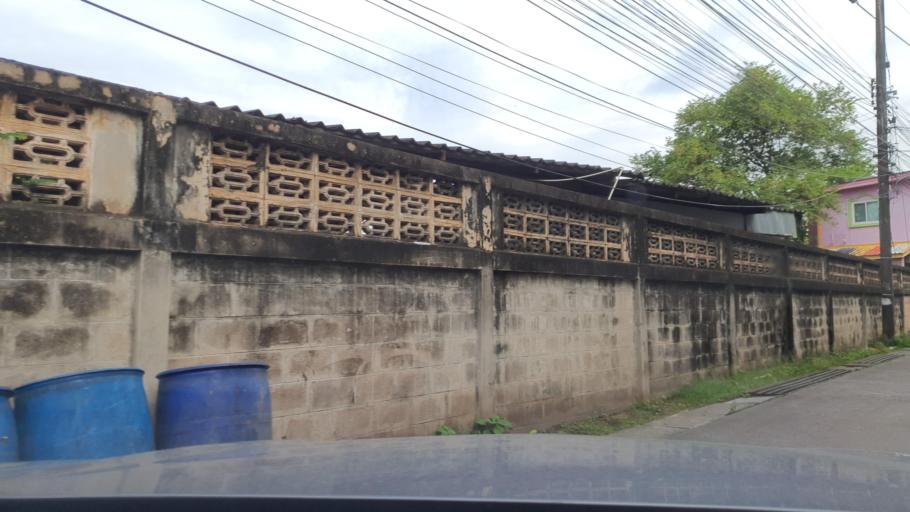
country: TH
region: Rayong
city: Rayong
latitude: 12.6853
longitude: 101.2738
